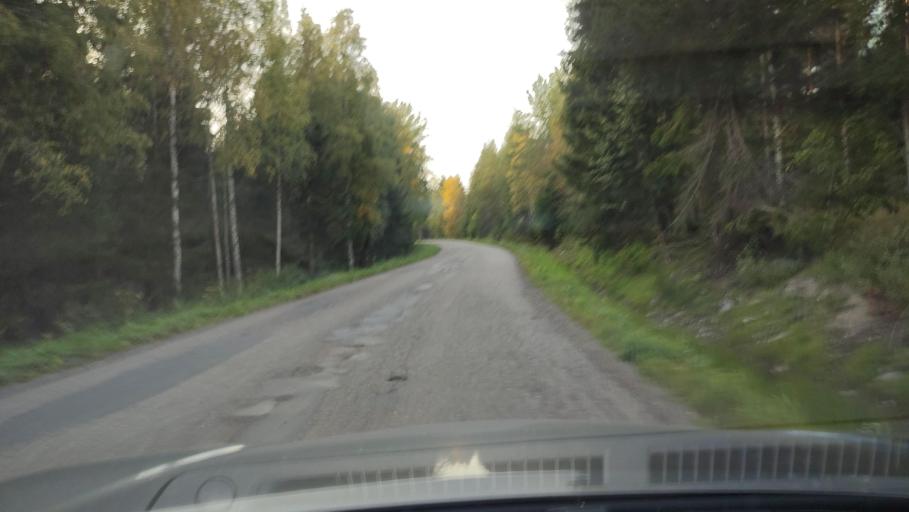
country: FI
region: Ostrobothnia
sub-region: Sydosterbotten
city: Kristinestad
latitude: 62.1531
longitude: 21.5320
